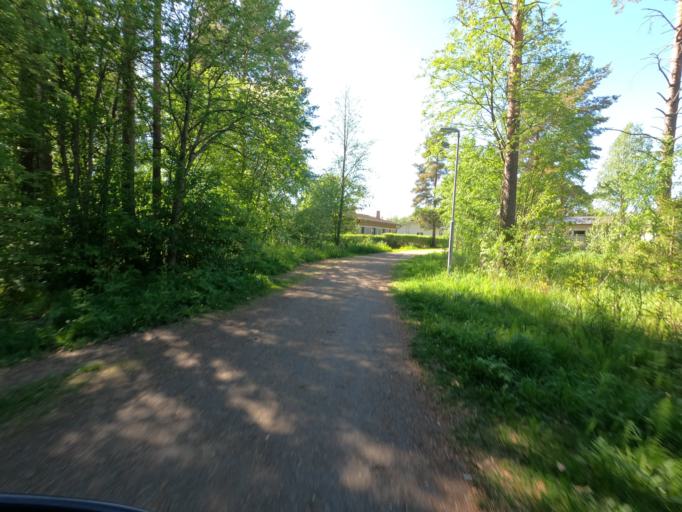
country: FI
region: North Karelia
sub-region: Joensuu
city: Joensuu
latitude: 62.5960
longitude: 29.8080
